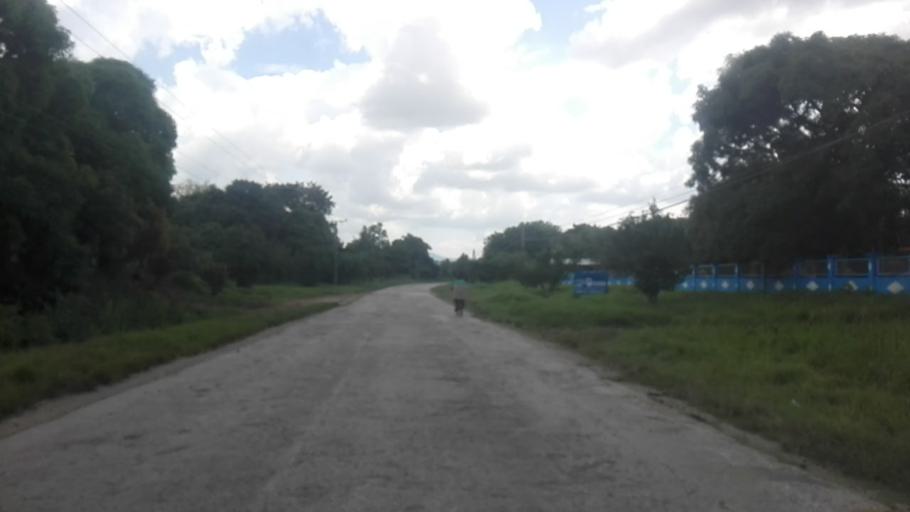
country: CU
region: Granma
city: Bartolome Maso
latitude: 20.1451
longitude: -76.9618
